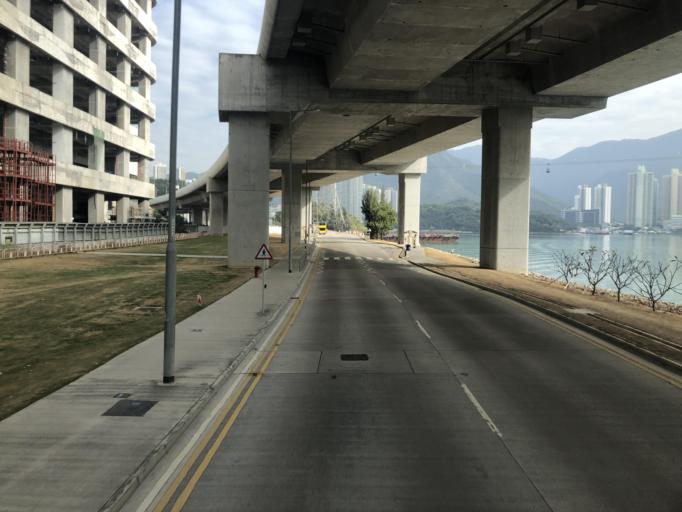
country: HK
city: Tai O
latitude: 22.2923
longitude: 113.9276
